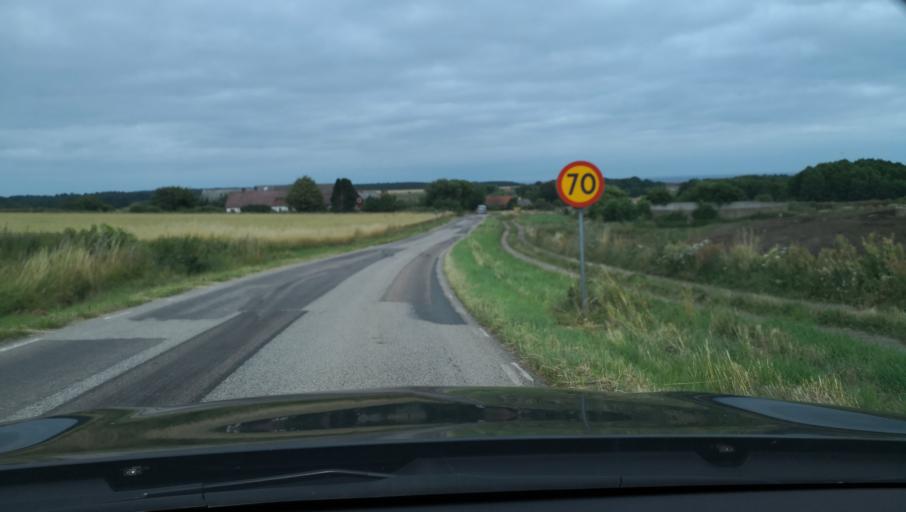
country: SE
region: Skane
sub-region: Simrishamns Kommun
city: Kivik
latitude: 55.6954
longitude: 14.1715
